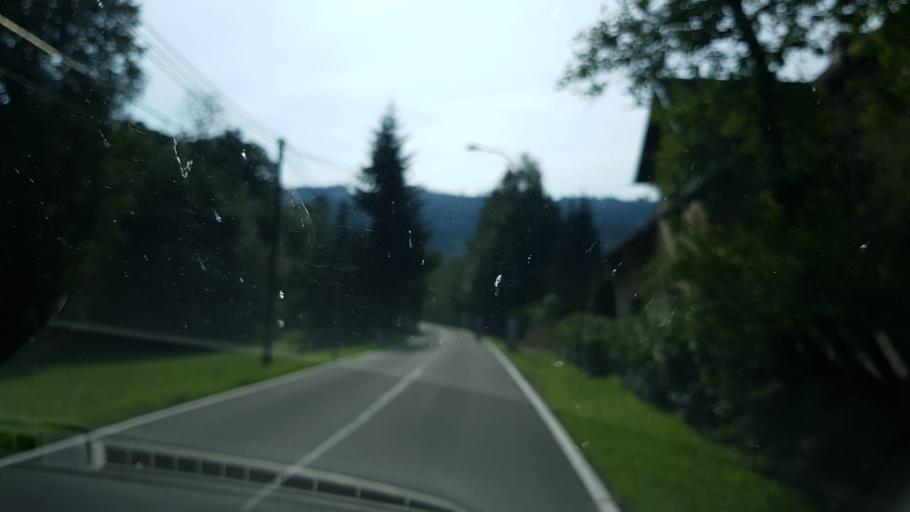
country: CZ
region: Olomoucky
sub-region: Okres Jesenik
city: Jesenik
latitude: 50.2085
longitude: 17.2301
